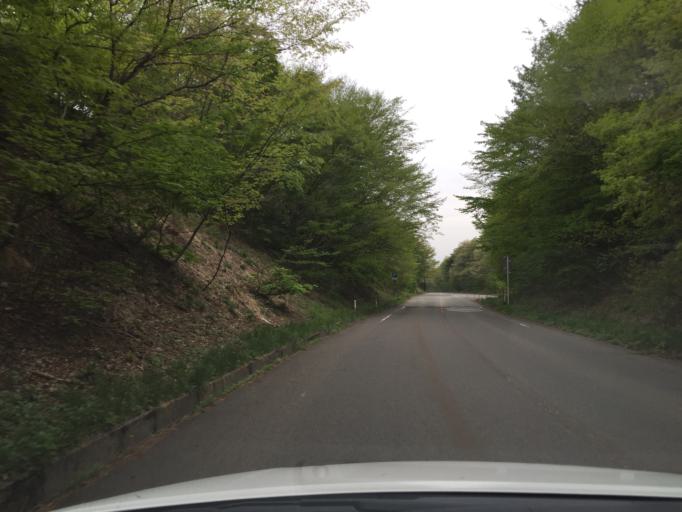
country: JP
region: Fukushima
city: Inawashiro
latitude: 37.5624
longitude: 140.2569
